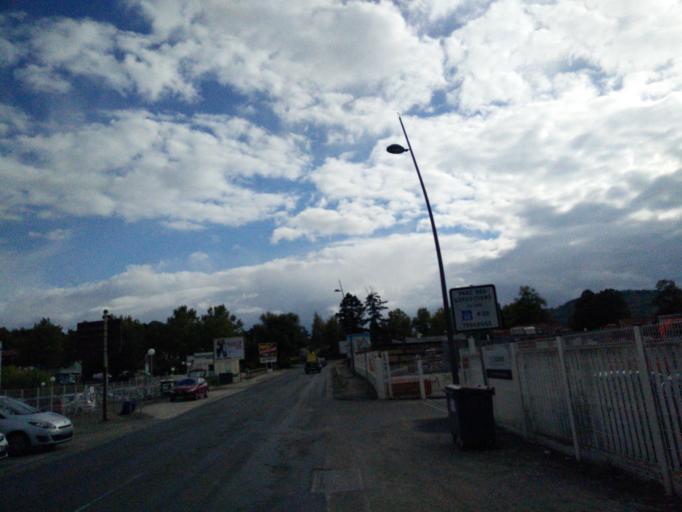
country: FR
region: Midi-Pyrenees
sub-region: Departement du Lot
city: Cahors
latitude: 44.4693
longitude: 1.4277
